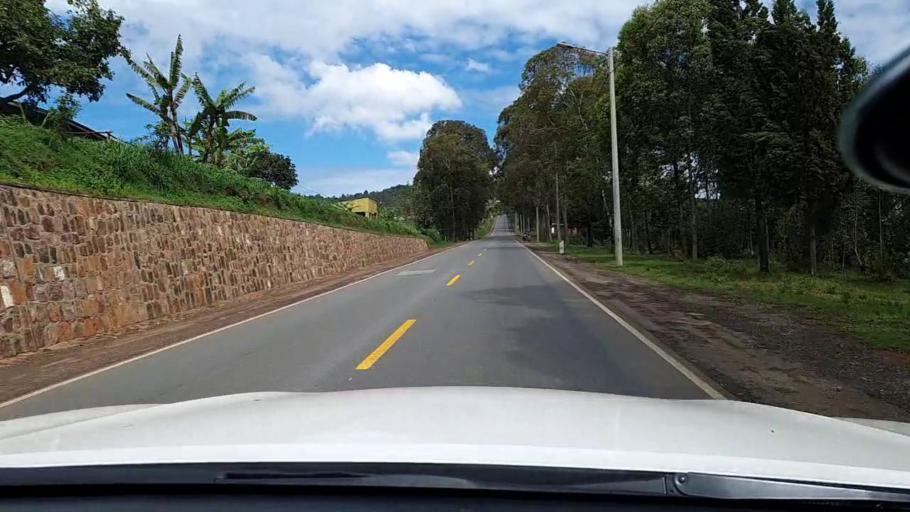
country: RW
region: Kigali
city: Kigali
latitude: -1.8347
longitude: 29.9518
